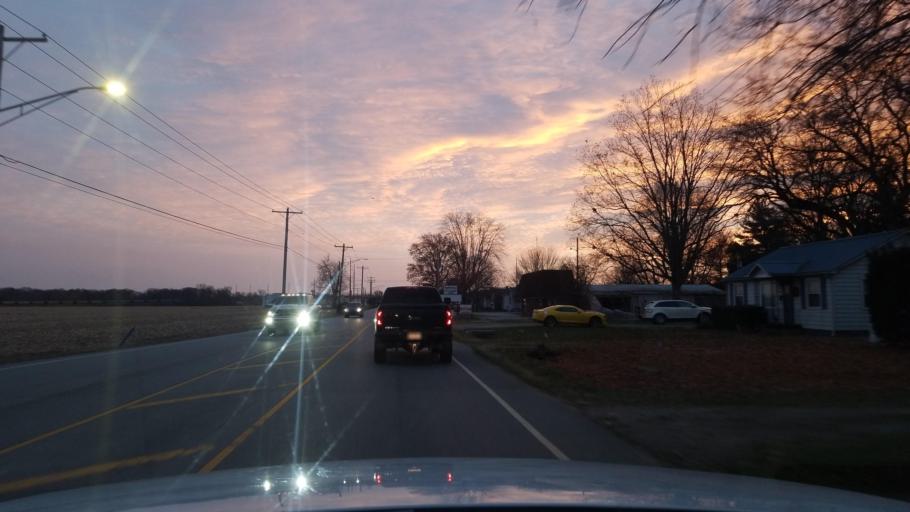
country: US
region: Indiana
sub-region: Posey County
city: Mount Vernon
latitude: 37.9355
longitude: -87.8827
